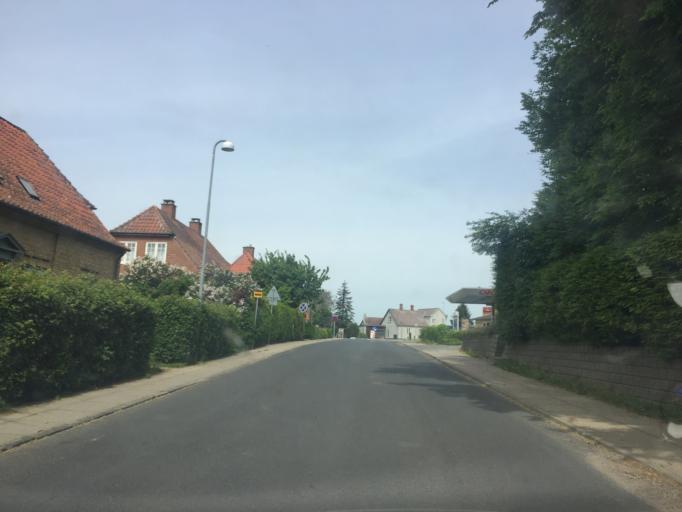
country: DK
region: South Denmark
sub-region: Svendborg Kommune
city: Svendborg
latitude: 55.0691
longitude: 10.5017
